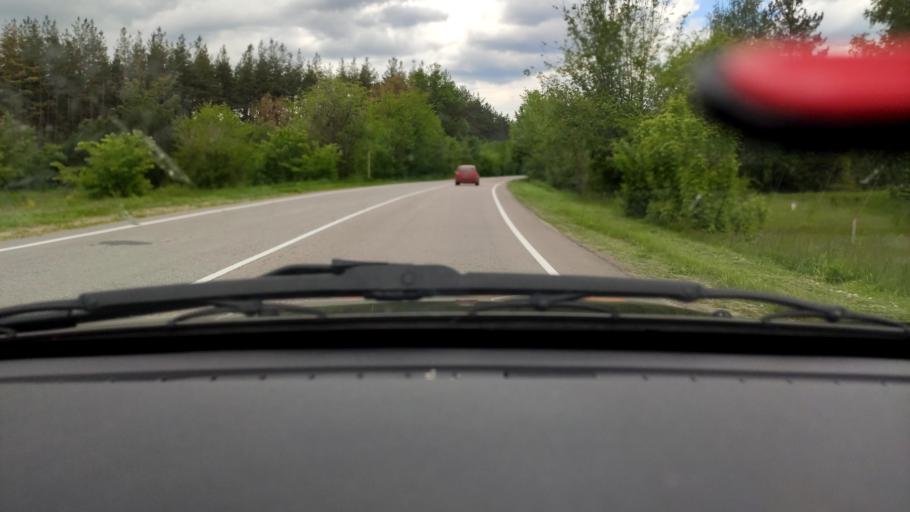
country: RU
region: Belgorod
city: Krasnoye
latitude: 51.0570
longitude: 38.8469
